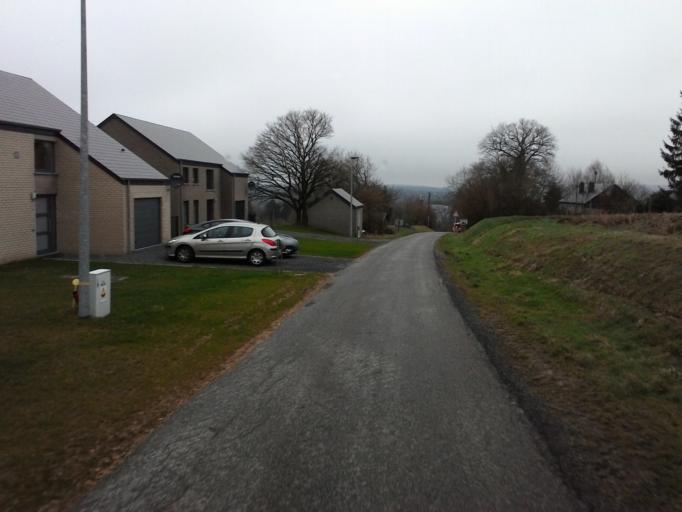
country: BE
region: Wallonia
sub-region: Province de Namur
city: Gedinne
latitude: 50.0182
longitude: 4.8671
